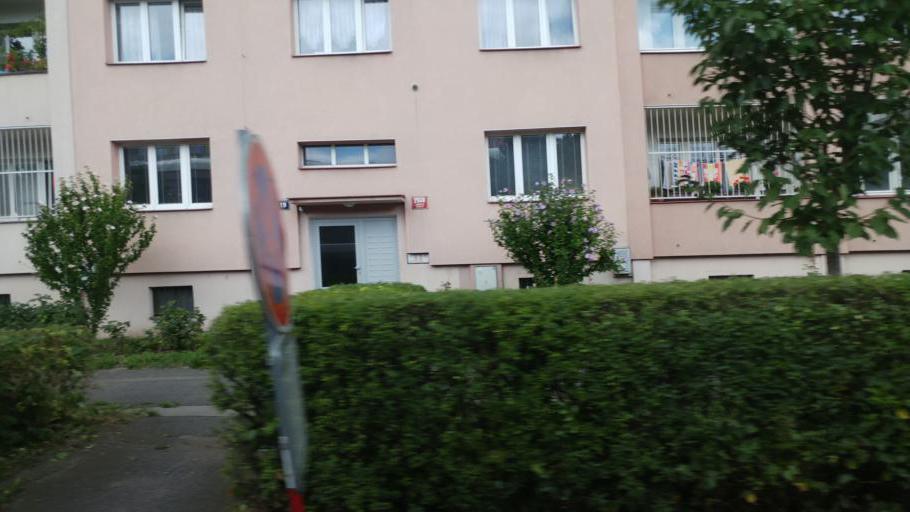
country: CZ
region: Praha
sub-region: Praha 9
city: Vysocany
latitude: 50.0572
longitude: 14.5070
